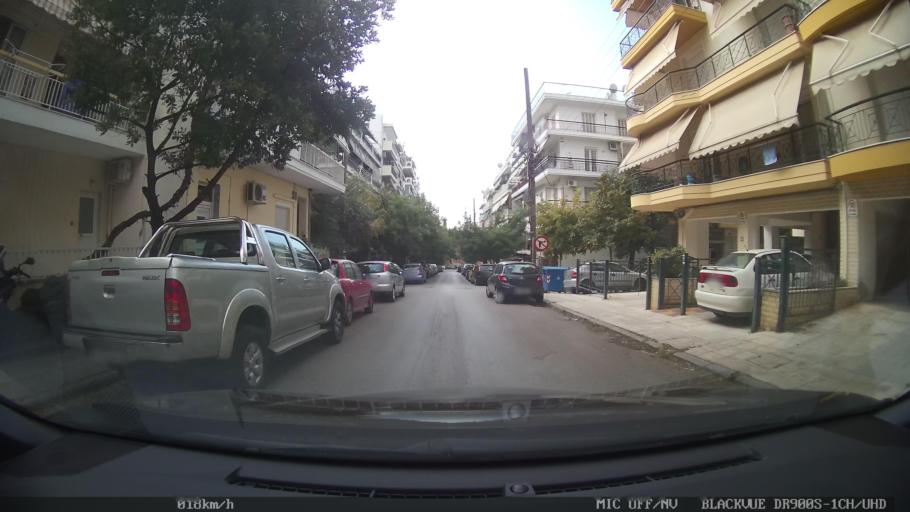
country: GR
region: Central Macedonia
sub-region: Nomos Thessalonikis
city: Triandria
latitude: 40.6143
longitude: 22.9816
